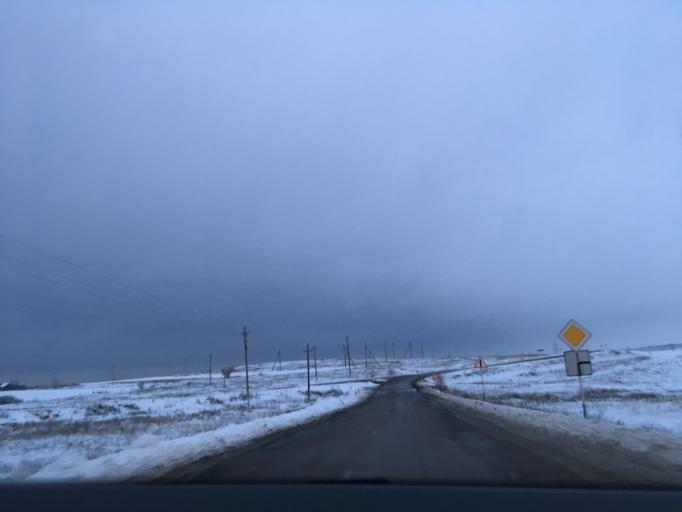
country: RU
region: Voronezj
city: Verkhniy Mamon
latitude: 50.0722
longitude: 40.3047
